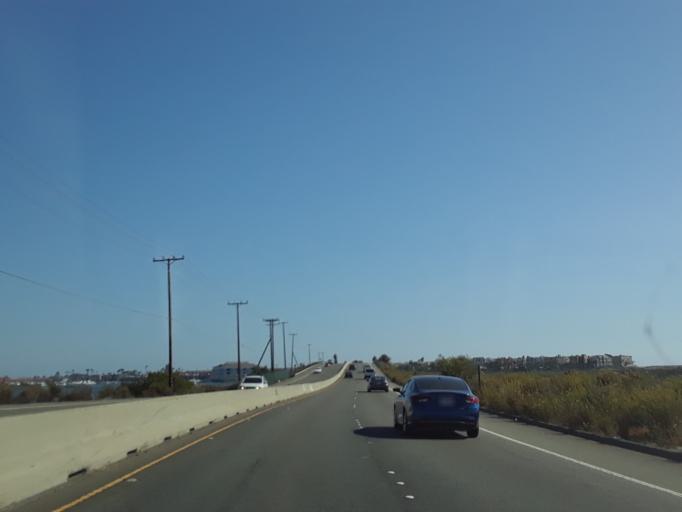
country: US
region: California
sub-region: Orange County
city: Seal Beach
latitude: 33.7356
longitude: -118.0863
